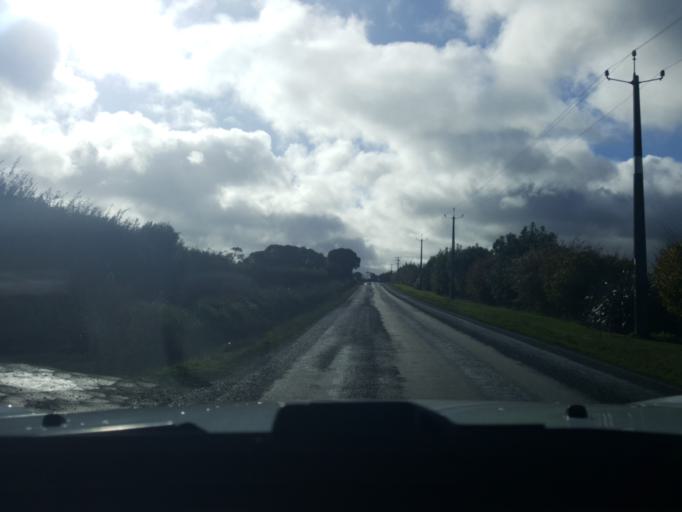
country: NZ
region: Auckland
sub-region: Auckland
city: Pukekohe East
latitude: -37.3032
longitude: 175.0169
